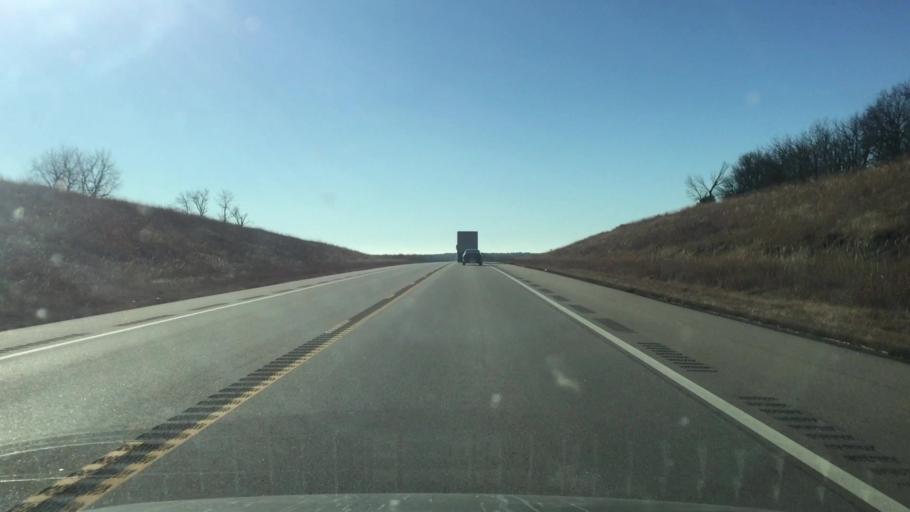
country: US
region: Kansas
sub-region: Allen County
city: Iola
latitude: 38.0123
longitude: -95.3807
